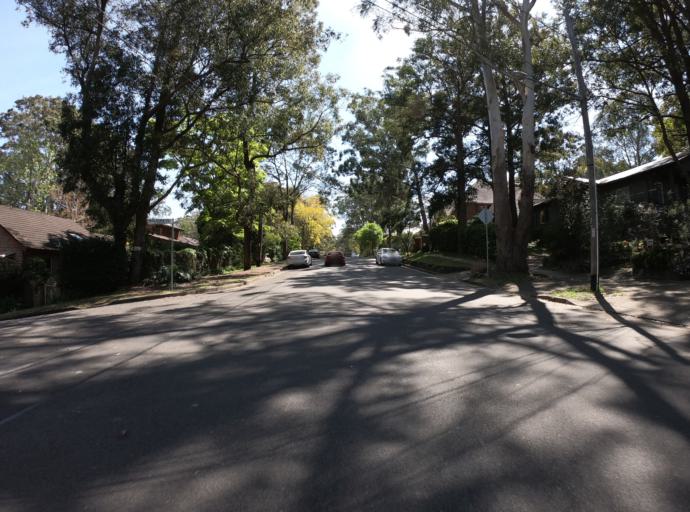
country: AU
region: New South Wales
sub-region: Hornsby Shire
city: Beecroft
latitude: -33.7499
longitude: 151.0582
